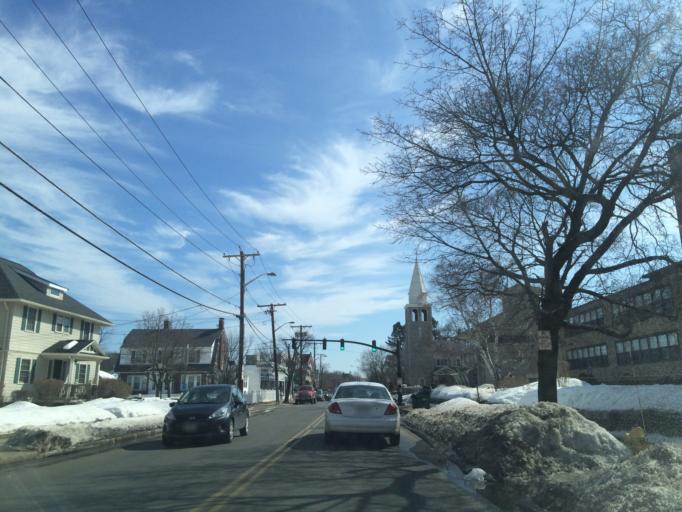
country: US
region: Massachusetts
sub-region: Middlesex County
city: Arlington
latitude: 42.4216
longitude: -71.1354
